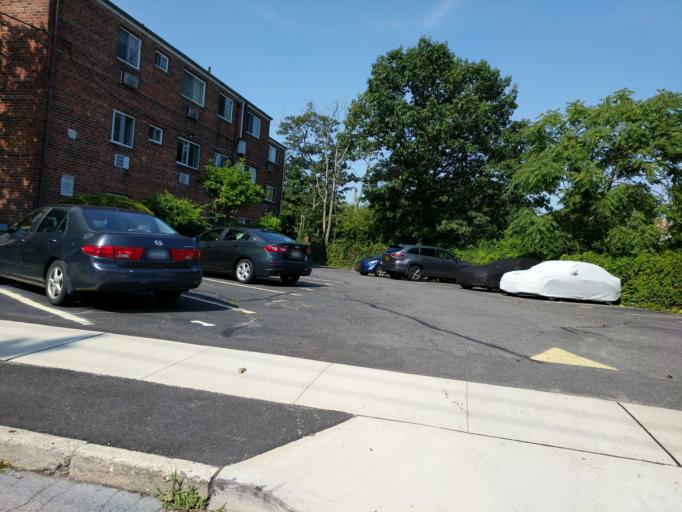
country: US
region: New York
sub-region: Nassau County
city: Hewlett
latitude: 40.6531
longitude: -73.7011
